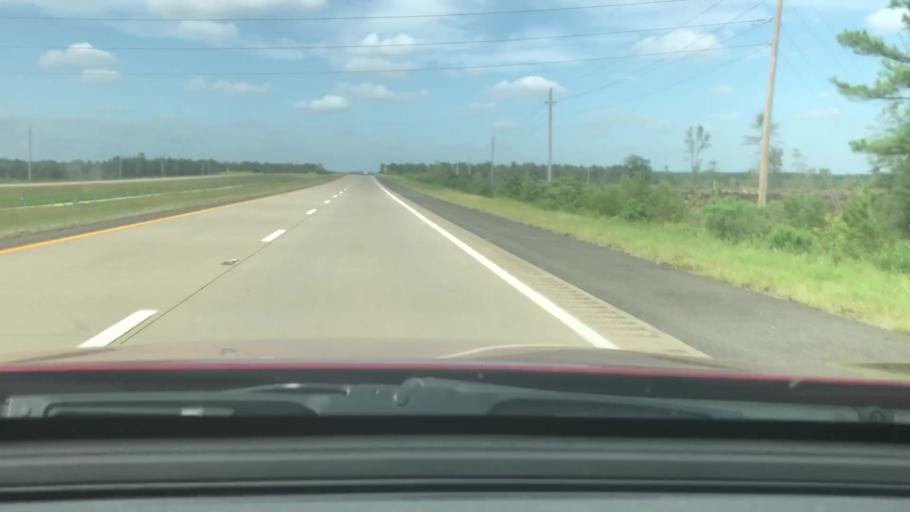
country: US
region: Texas
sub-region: Bowie County
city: Texarkana
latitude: 33.2208
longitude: -93.8733
